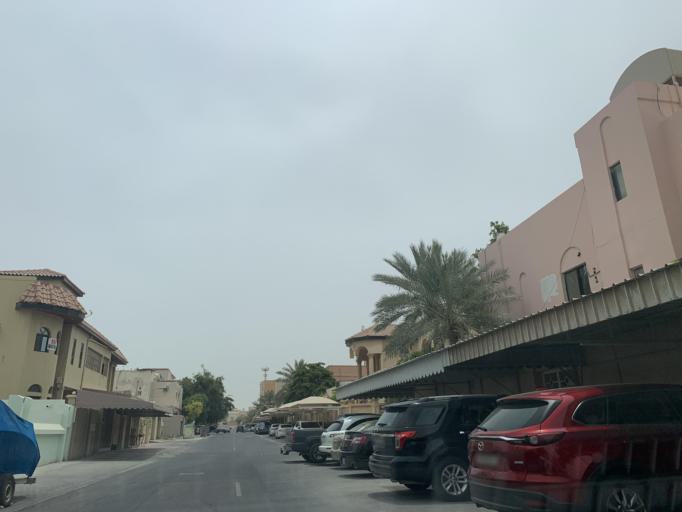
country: BH
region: Northern
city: Ar Rifa'
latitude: 26.1383
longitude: 50.5614
